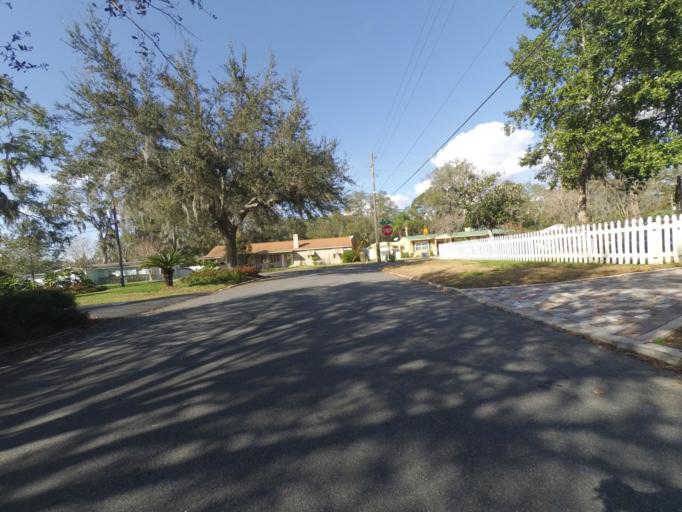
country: US
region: Florida
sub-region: Lake County
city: Mount Dora
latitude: 28.8057
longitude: -81.6478
